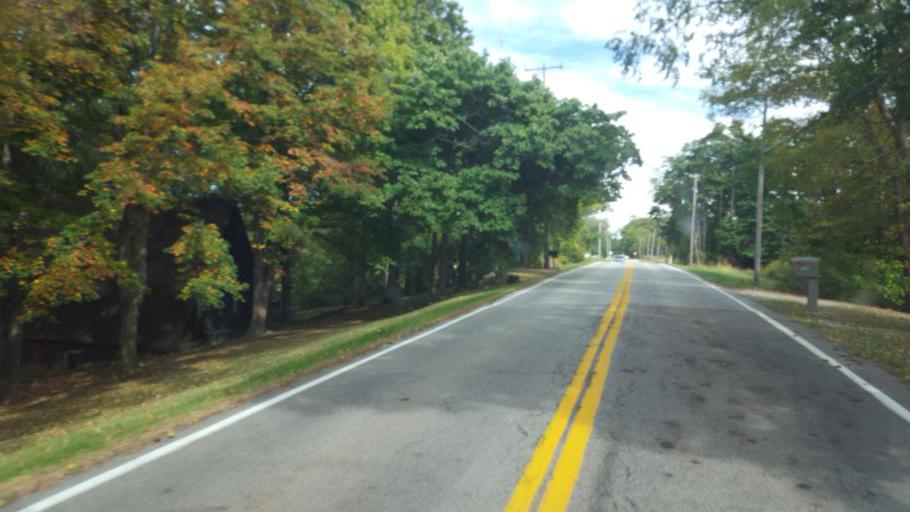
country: US
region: Ohio
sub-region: Lorain County
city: South Amherst
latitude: 41.3916
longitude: -82.2702
